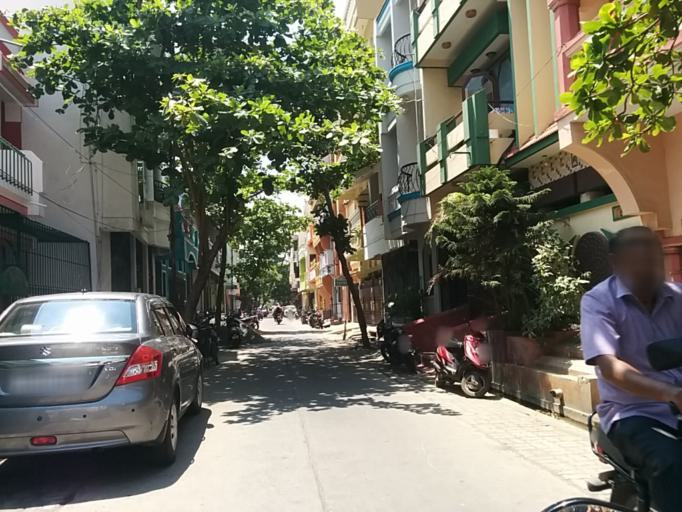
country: IN
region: Pondicherry
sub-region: Puducherry
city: Puducherry
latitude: 11.9283
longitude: 79.8289
